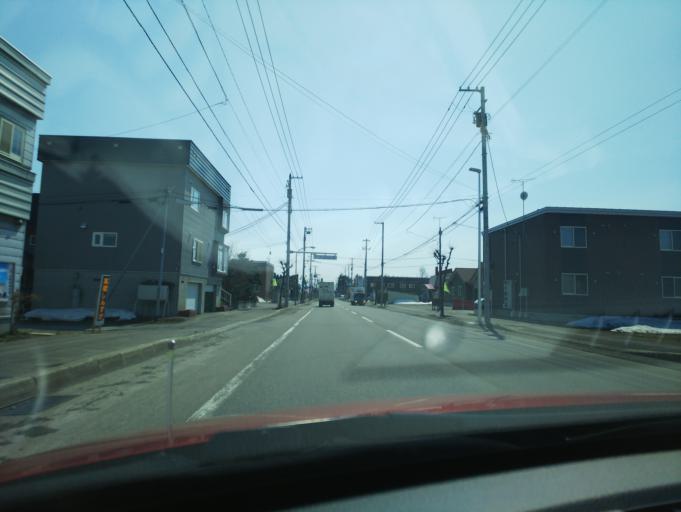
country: JP
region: Hokkaido
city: Nayoro
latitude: 44.3423
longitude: 142.4643
